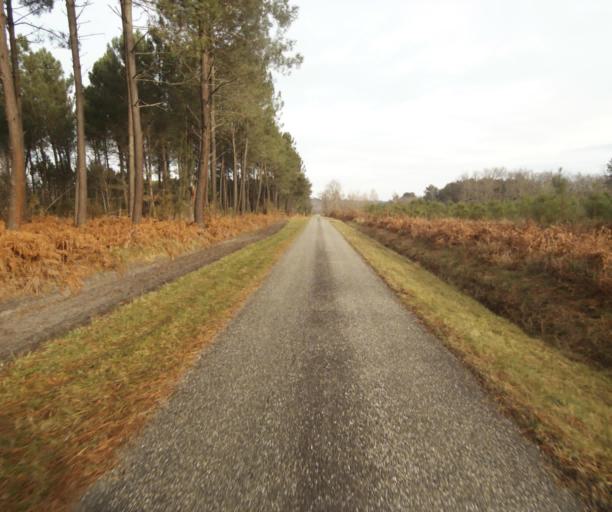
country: FR
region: Aquitaine
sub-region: Departement des Landes
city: Gabarret
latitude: 44.0722
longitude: 0.0767
